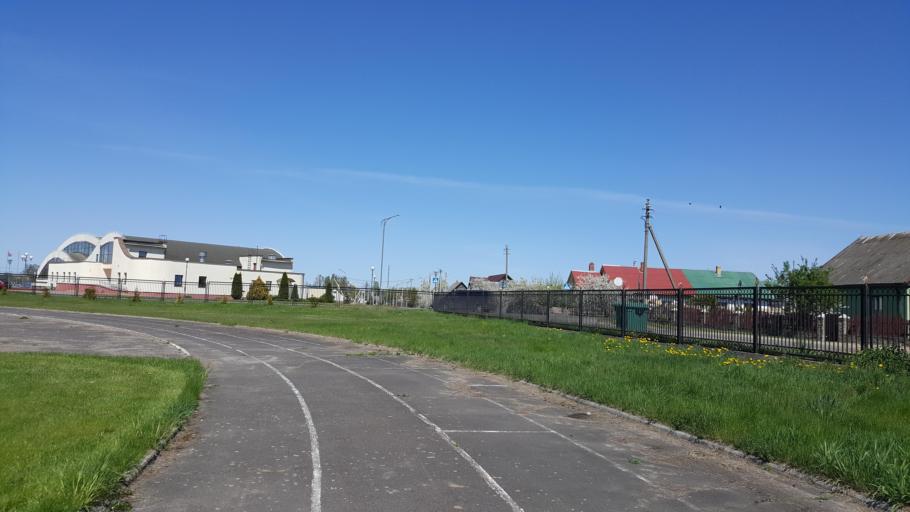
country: BY
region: Brest
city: Kamyanyets
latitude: 52.3989
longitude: 23.8123
